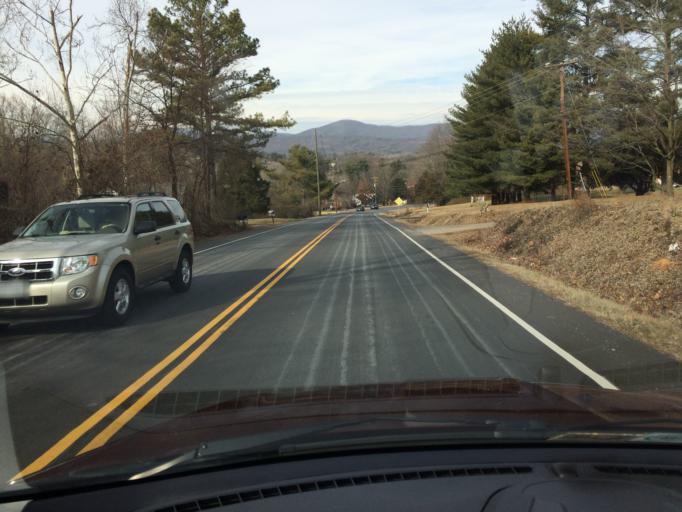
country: US
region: Virginia
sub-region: Roanoke County
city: Hollins
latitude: 37.3415
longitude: -79.9438
